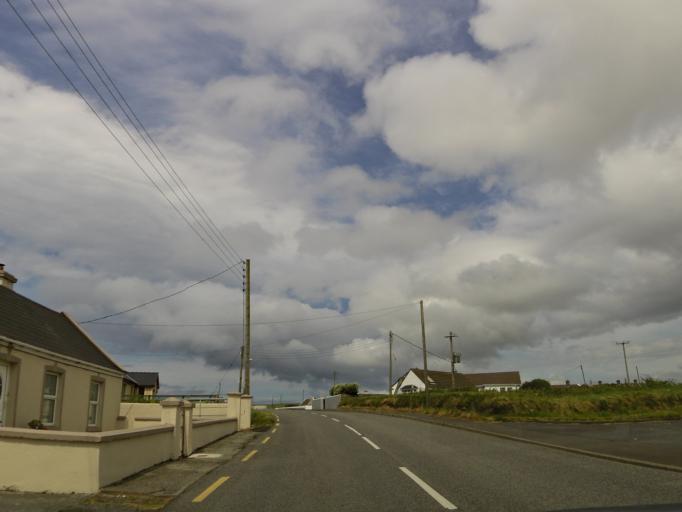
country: IE
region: Munster
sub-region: An Clar
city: Kilrush
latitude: 52.6857
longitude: -9.6416
